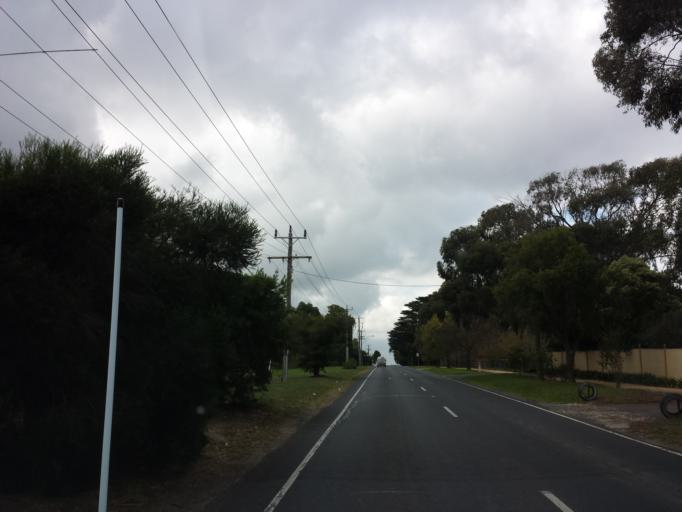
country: AU
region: Victoria
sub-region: Casey
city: Narre Warren South
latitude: -38.0557
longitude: 145.3055
